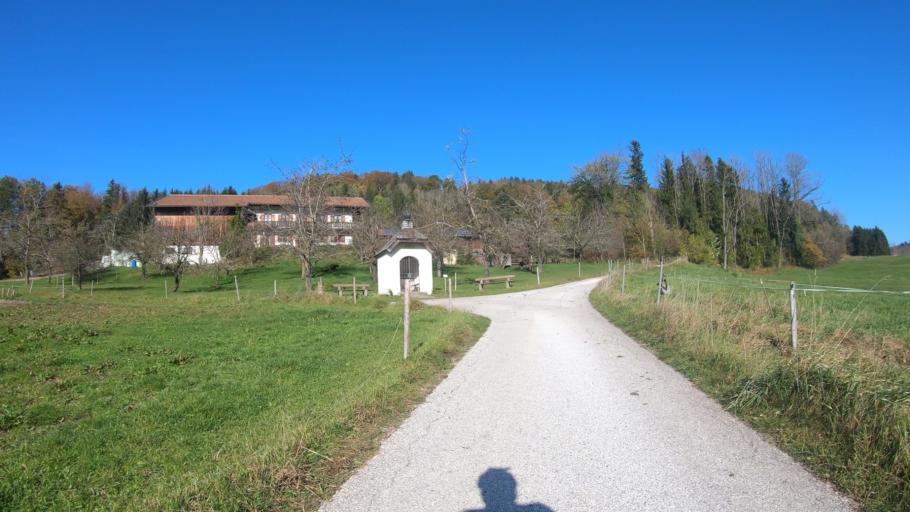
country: DE
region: Bavaria
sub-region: Upper Bavaria
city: Bergen
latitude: 47.8054
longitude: 12.6021
